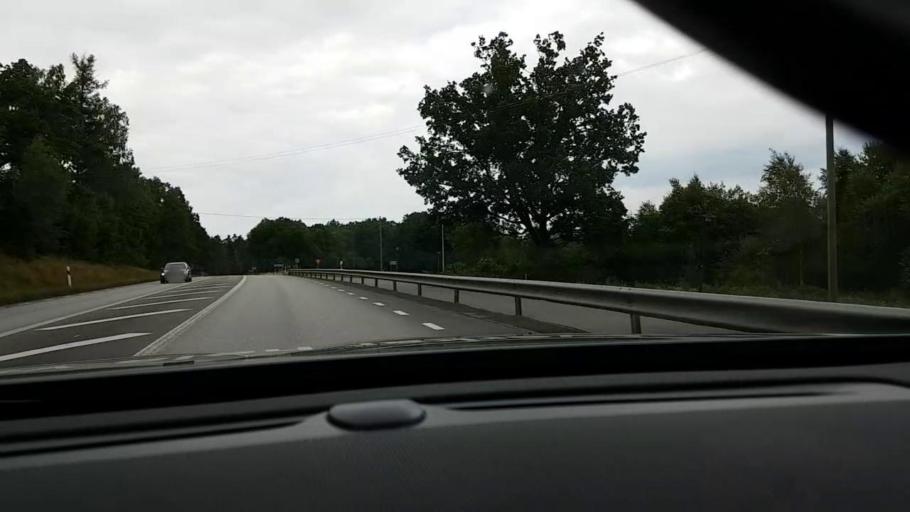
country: SE
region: Skane
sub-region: Hassleholms Kommun
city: Tormestorp
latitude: 56.0628
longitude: 13.7356
